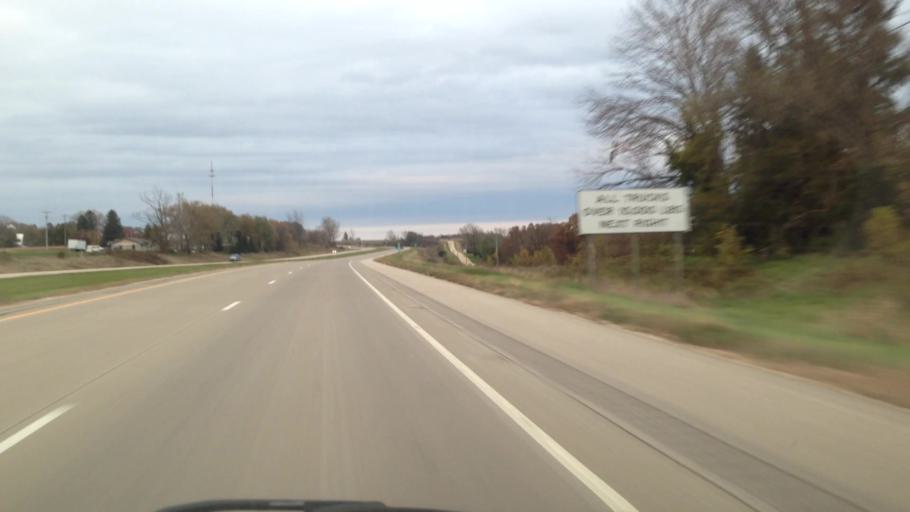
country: US
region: Minnesota
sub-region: Winona County
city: Winona
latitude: 43.9128
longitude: -91.5712
